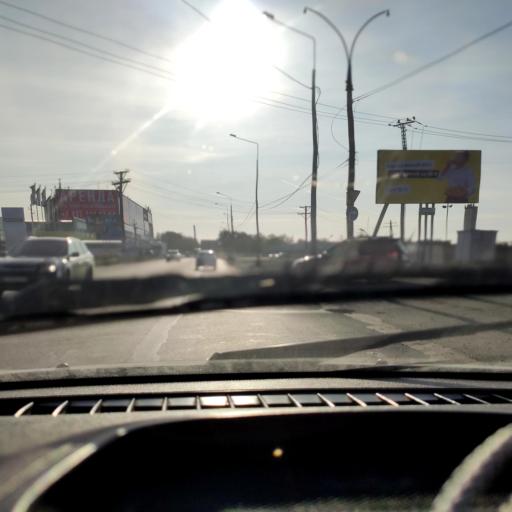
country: RU
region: Samara
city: Tol'yatti
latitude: 53.5711
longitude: 49.4596
